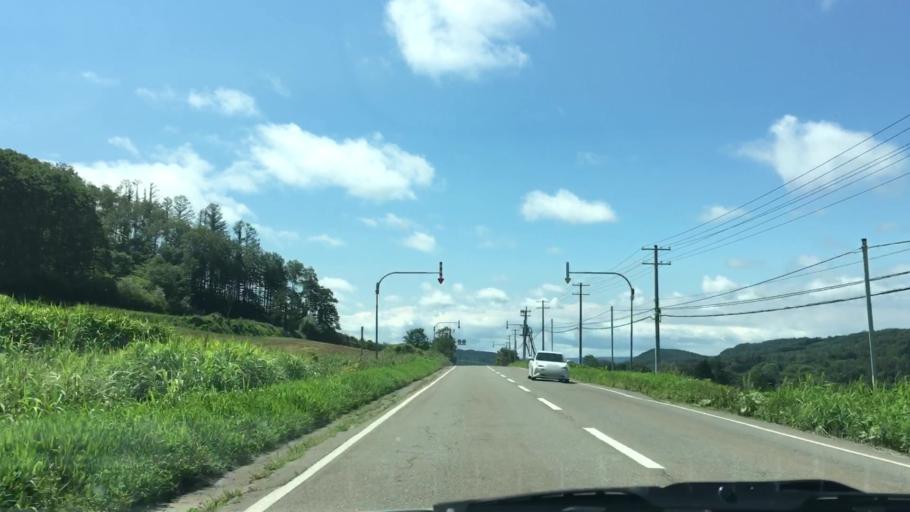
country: JP
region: Hokkaido
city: Kitami
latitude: 43.3134
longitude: 143.7170
